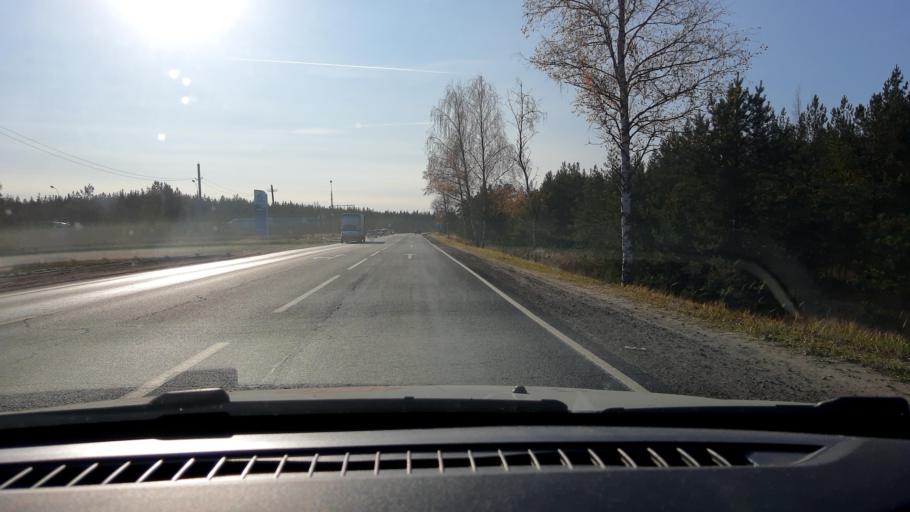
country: RU
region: Nizjnij Novgorod
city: Dzerzhinsk
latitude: 56.2783
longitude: 43.4751
